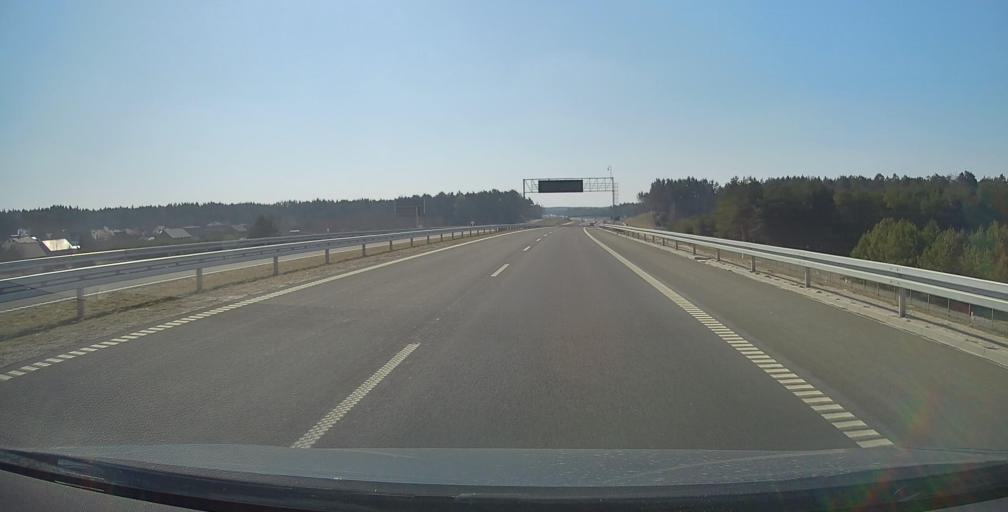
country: PL
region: Subcarpathian Voivodeship
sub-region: Powiat nizanski
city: Jarocin
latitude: 50.6369
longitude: 22.2885
